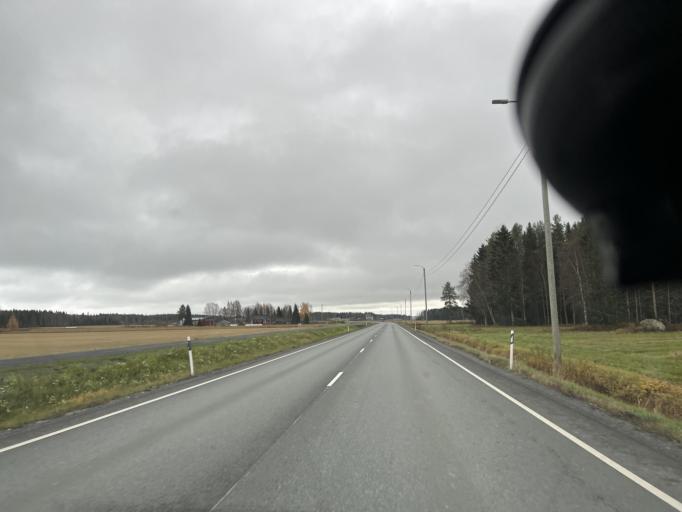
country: FI
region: Northern Ostrobothnia
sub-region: Ylivieska
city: Sievi
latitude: 63.9576
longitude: 24.5061
